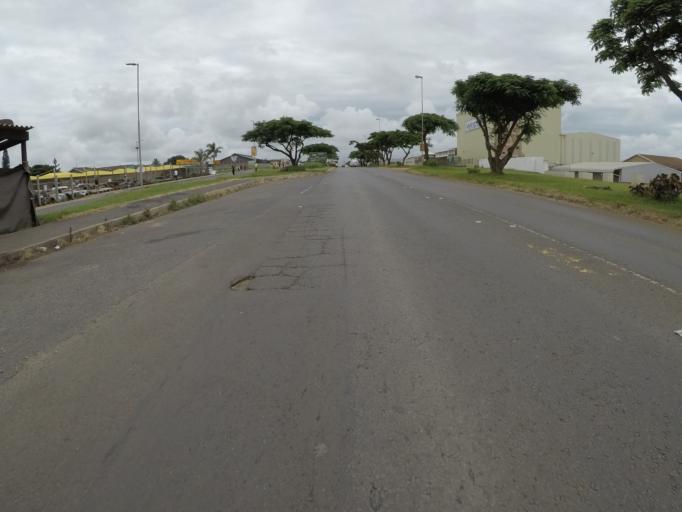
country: ZA
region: KwaZulu-Natal
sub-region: uThungulu District Municipality
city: Empangeni
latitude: -28.7755
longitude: 31.9006
